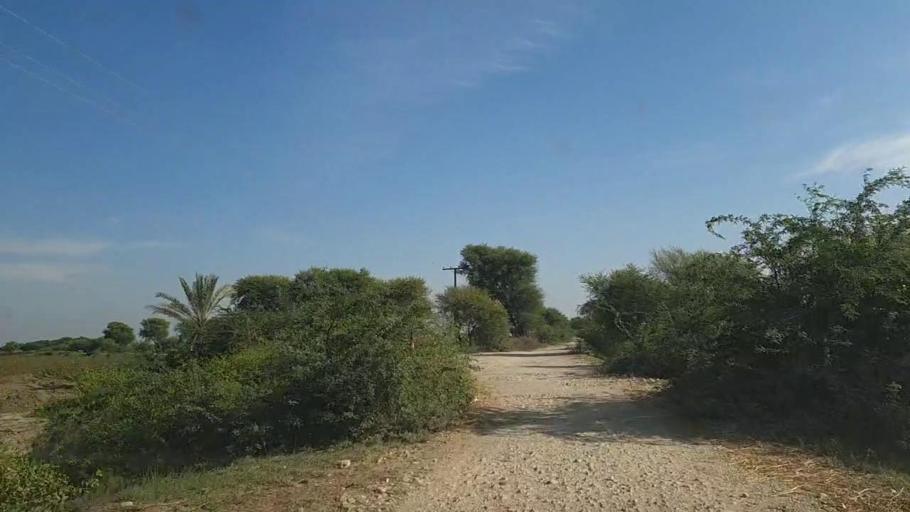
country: PK
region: Sindh
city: Bulri
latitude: 24.8010
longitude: 68.3349
